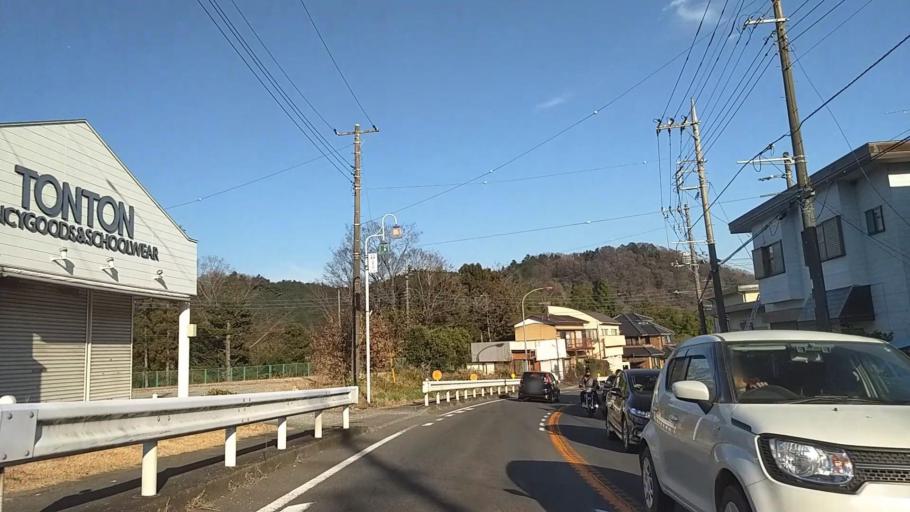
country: JP
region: Kanagawa
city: Zama
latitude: 35.5334
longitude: 139.2801
